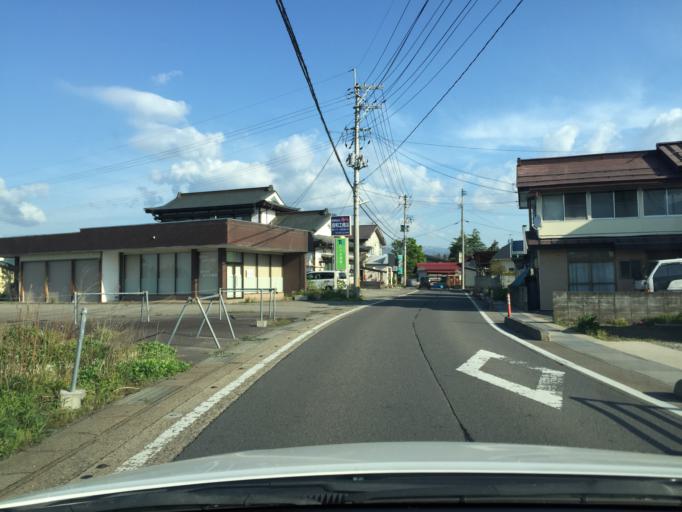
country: JP
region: Fukushima
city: Kitakata
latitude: 37.6758
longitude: 139.8715
